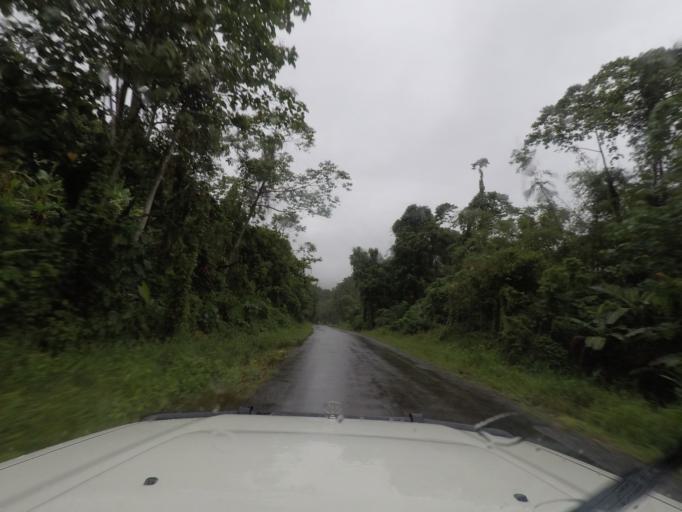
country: PG
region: Madang
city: Madang
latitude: -5.3983
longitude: 145.6197
